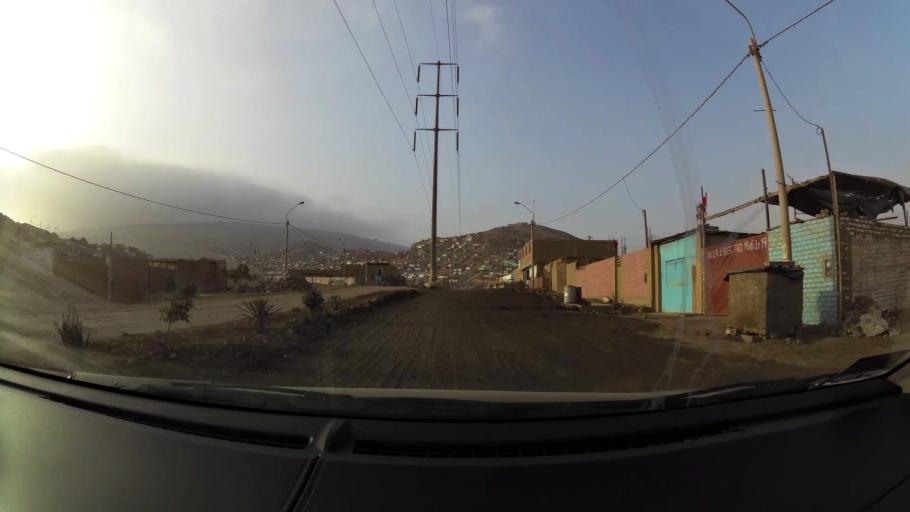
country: PE
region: Lima
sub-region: Lima
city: Santa Rosa
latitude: -11.7468
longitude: -77.1513
